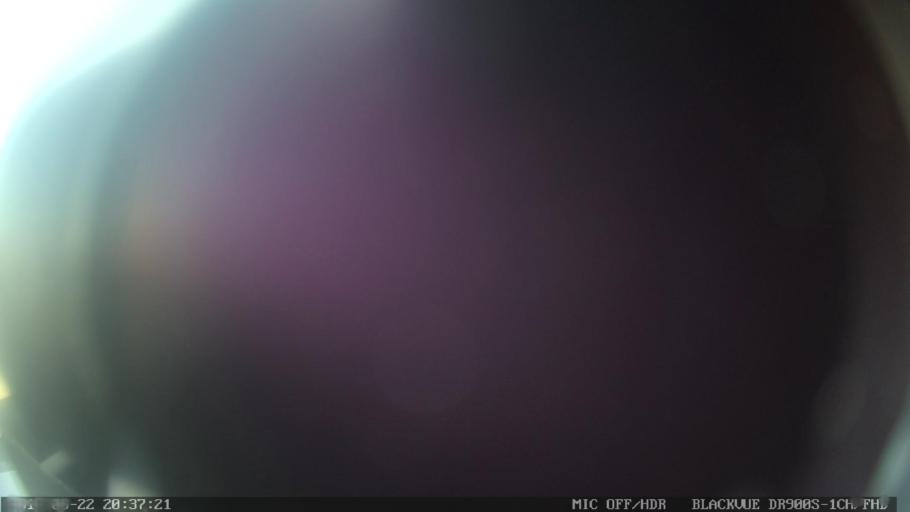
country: PT
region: Portalegre
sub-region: Nisa
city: Nisa
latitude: 39.6739
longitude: -7.7332
